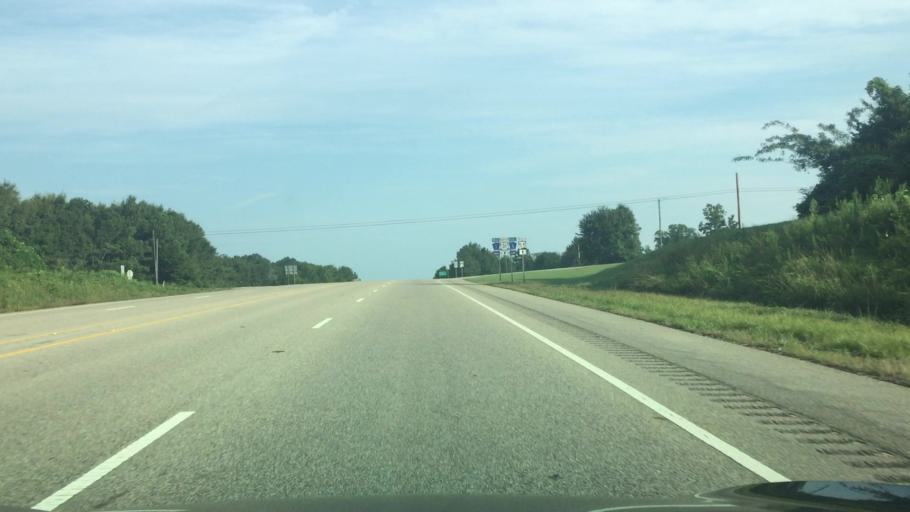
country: US
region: Alabama
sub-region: Butler County
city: Georgiana
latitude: 31.5396
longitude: -86.7277
